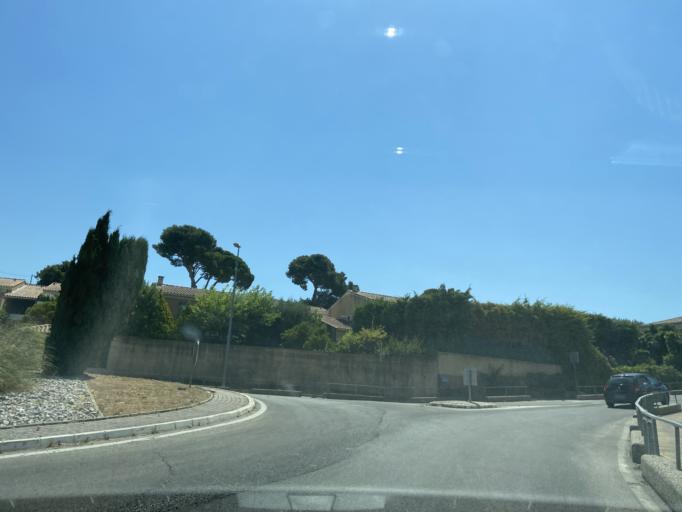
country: FR
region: Provence-Alpes-Cote d'Azur
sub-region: Departement des Bouches-du-Rhone
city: Plan-de-Cuques
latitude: 43.3428
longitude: 5.4488
